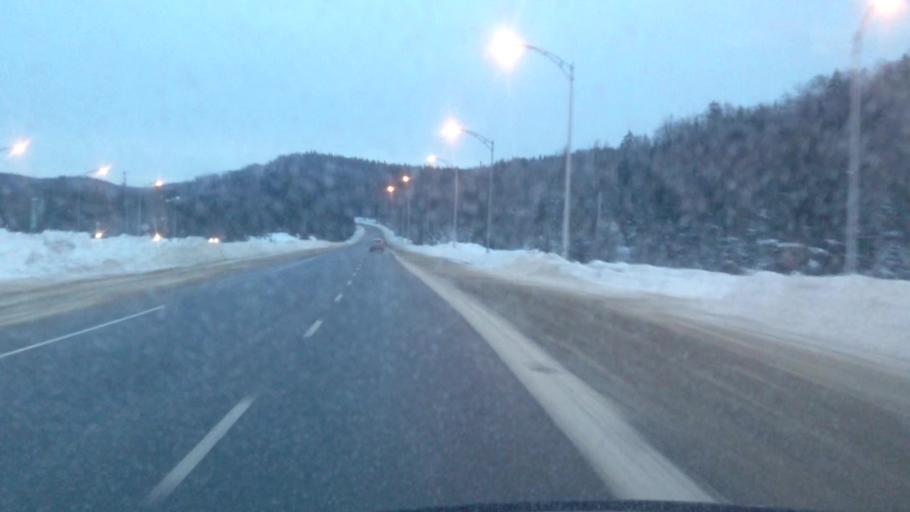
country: CA
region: Quebec
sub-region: Laurentides
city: Sainte-Agathe-des-Monts
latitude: 46.1183
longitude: -74.4319
